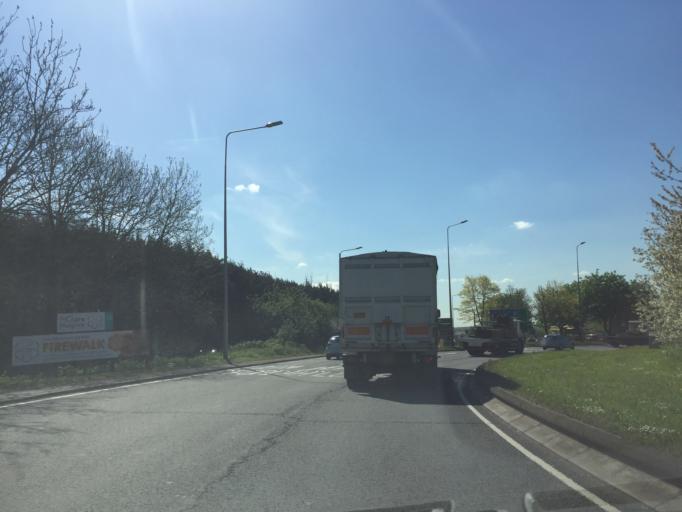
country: GB
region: England
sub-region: Essex
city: Harlow
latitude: 51.7434
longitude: 0.1394
